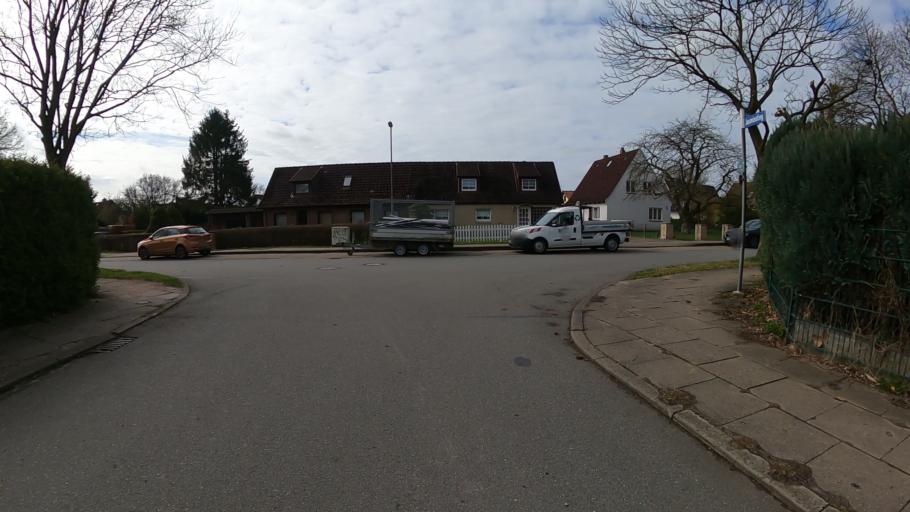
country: DE
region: Schleswig-Holstein
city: Ahrensburg
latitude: 53.6391
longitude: 10.2163
